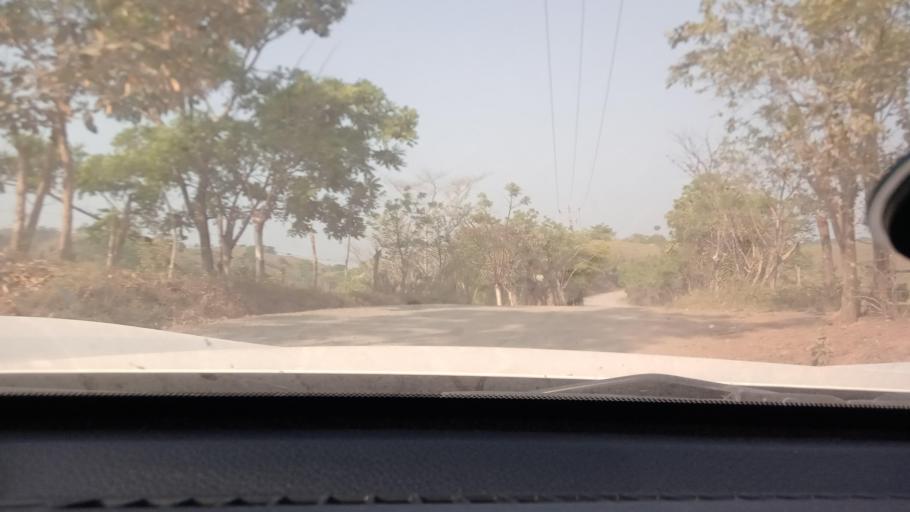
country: MX
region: Tabasco
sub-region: Huimanguillo
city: Francisco Rueda
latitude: 17.6534
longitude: -93.8985
